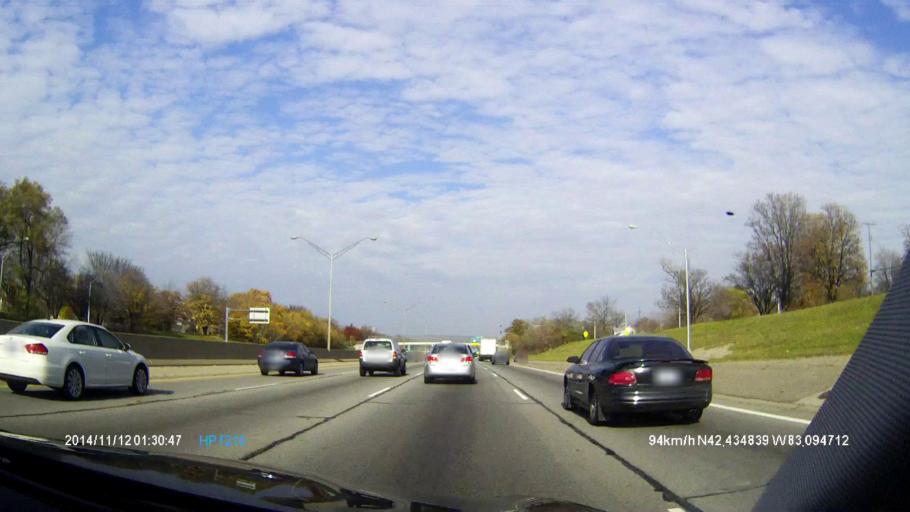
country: US
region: Michigan
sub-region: Wayne County
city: Highland Park
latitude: 42.4348
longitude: -83.0947
